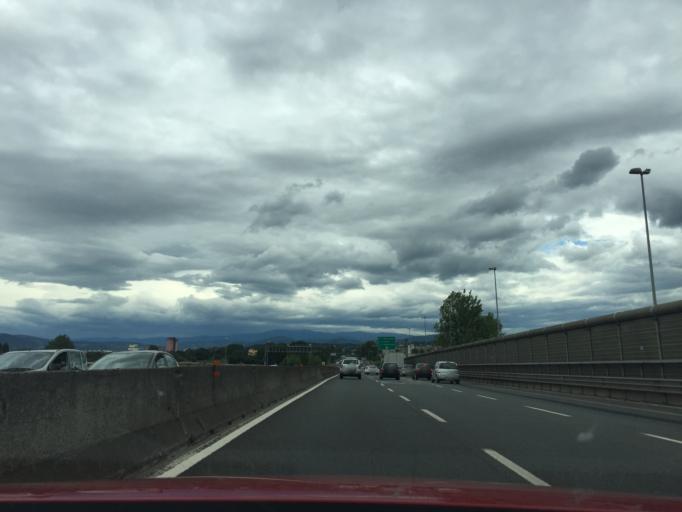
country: IT
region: Tuscany
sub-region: Province of Florence
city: Mantignano-Ugnano
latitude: 43.7726
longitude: 11.1639
